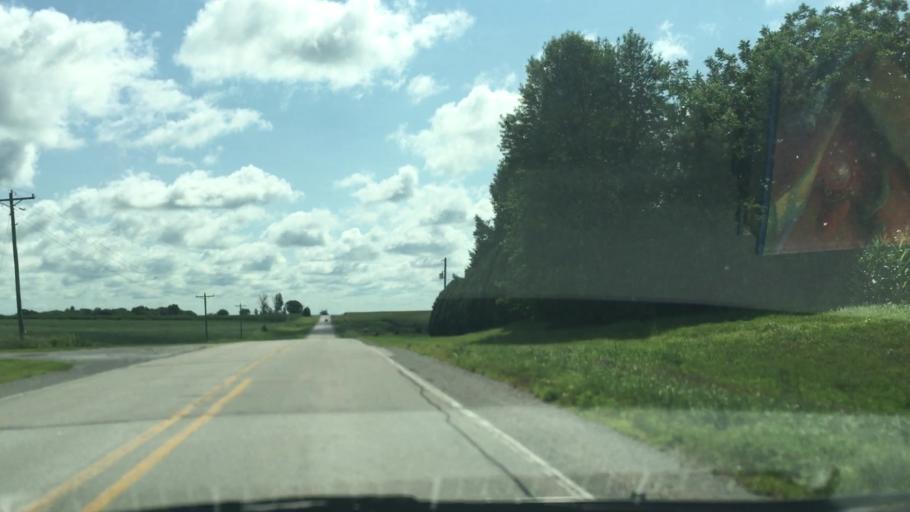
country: US
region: Iowa
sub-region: Johnson County
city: Solon
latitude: 41.8310
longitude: -91.4545
